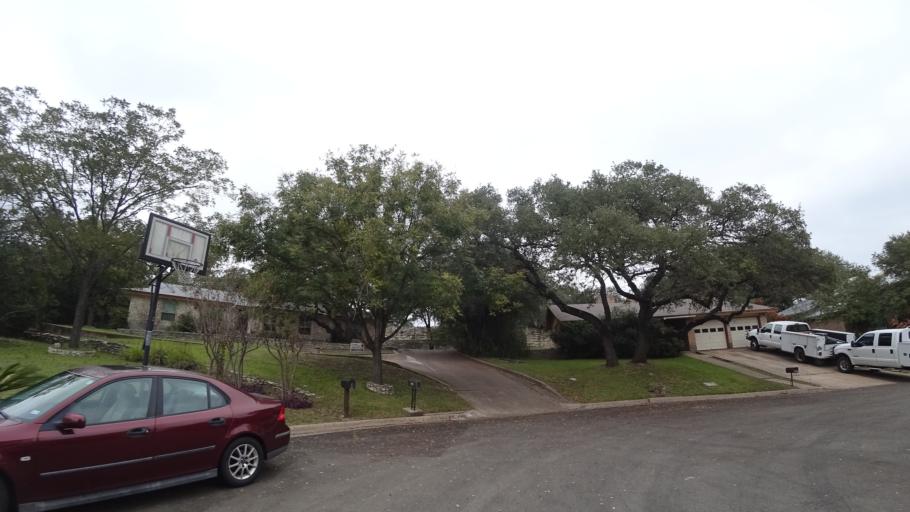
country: US
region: Texas
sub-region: Travis County
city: Barton Creek
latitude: 30.2382
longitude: -97.8845
